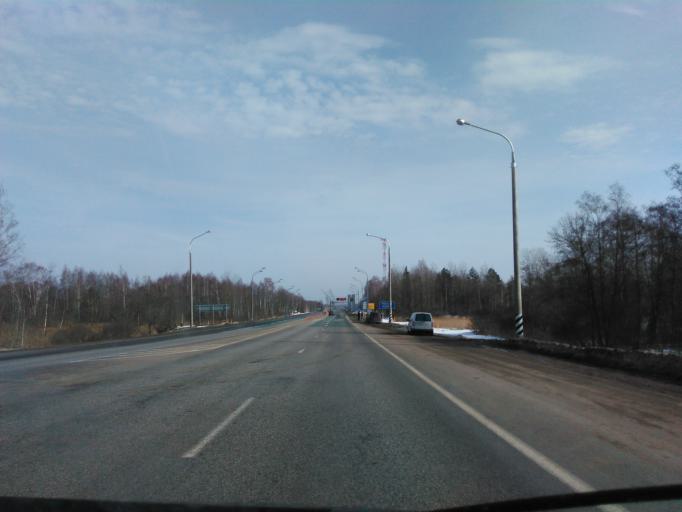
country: RU
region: Smolensk
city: Rudnya
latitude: 54.6906
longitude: 30.9824
